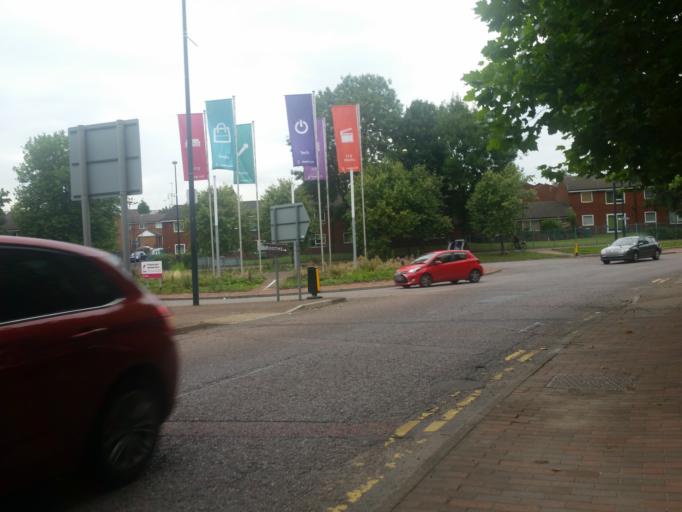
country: GB
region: England
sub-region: City and Borough of Salford
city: Salford
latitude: 53.4754
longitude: -2.2866
